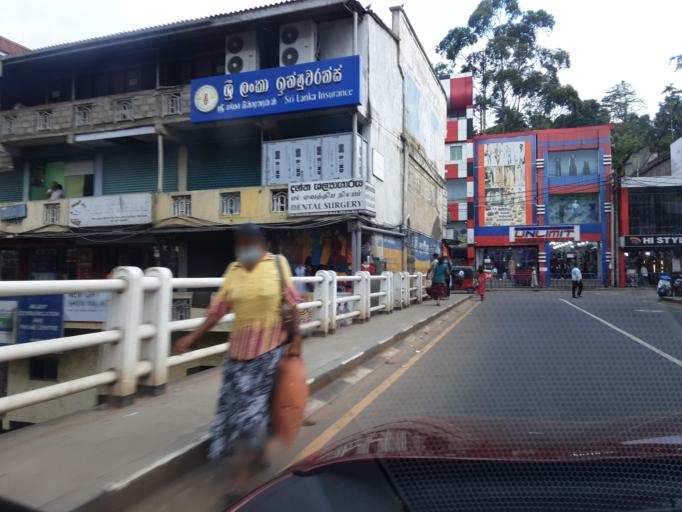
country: LK
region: Central
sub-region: Nuwara Eliya District
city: Nuwara Eliya
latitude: 6.9052
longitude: 80.9120
